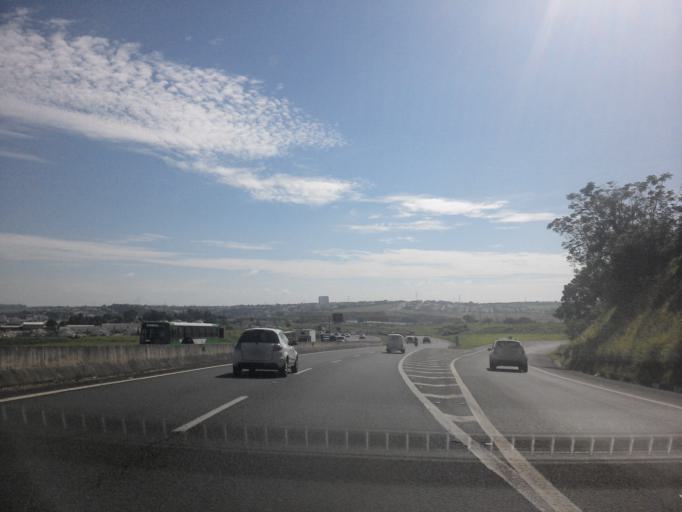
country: BR
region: Sao Paulo
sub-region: Campinas
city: Campinas
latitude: -22.8462
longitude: -47.0405
